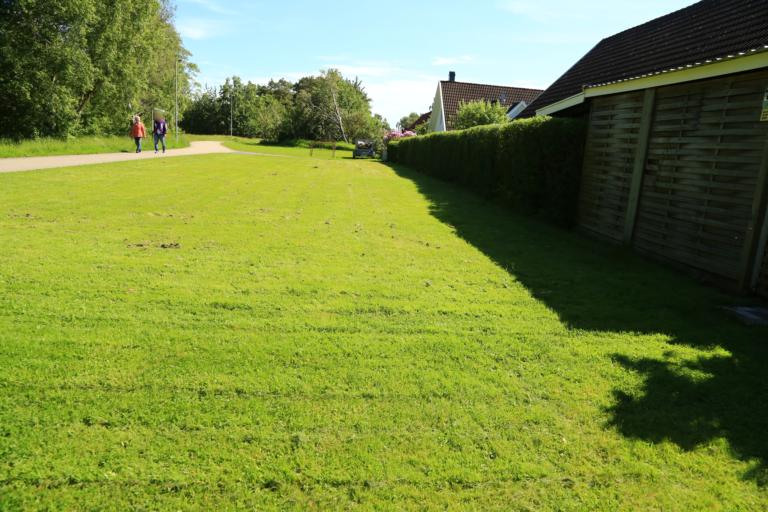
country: SE
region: Halland
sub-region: Varbergs Kommun
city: Traslovslage
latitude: 57.1037
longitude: 12.2939
